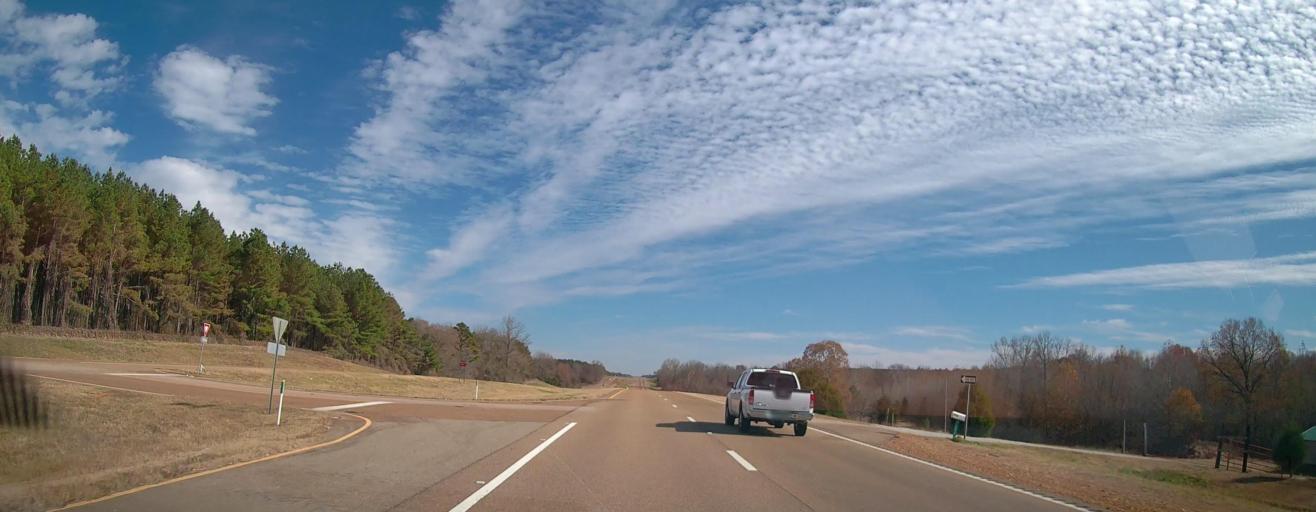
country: US
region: Mississippi
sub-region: Benton County
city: Ashland
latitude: 34.9480
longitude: -89.1123
